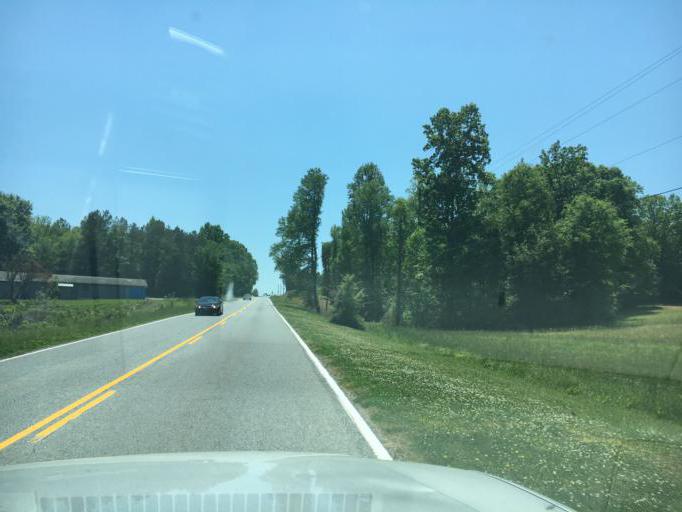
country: US
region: South Carolina
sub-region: Cherokee County
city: East Gaffney
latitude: 35.1159
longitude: -81.6003
